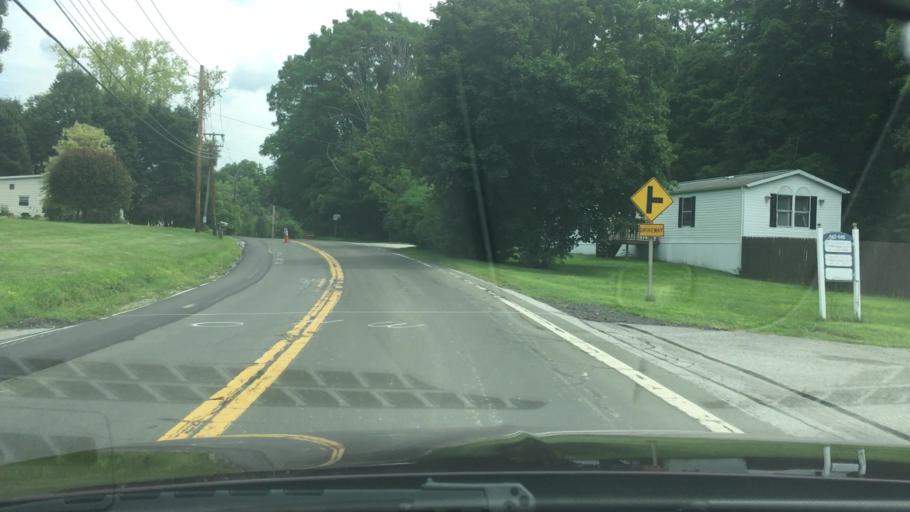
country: US
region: New York
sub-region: Dutchess County
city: Hillside Lake
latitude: 41.5853
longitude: -73.7155
